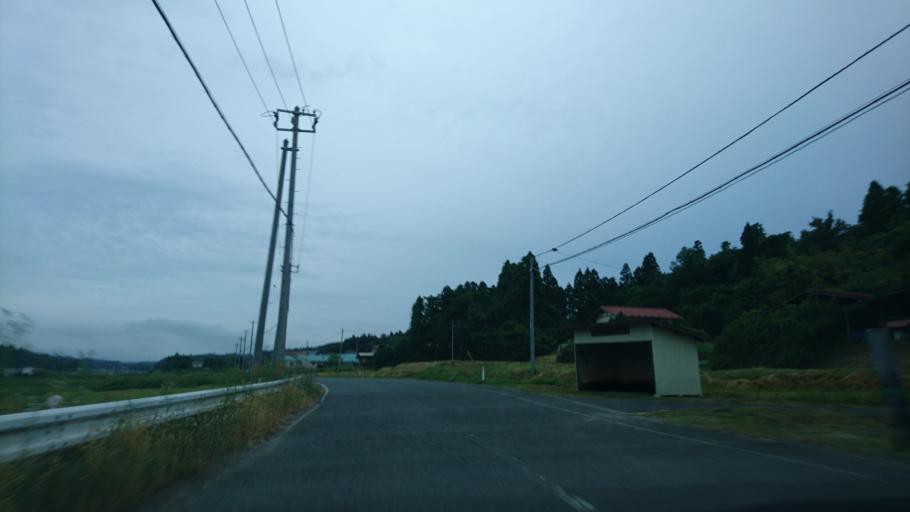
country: JP
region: Iwate
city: Ichinoseki
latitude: 38.9315
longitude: 141.1724
